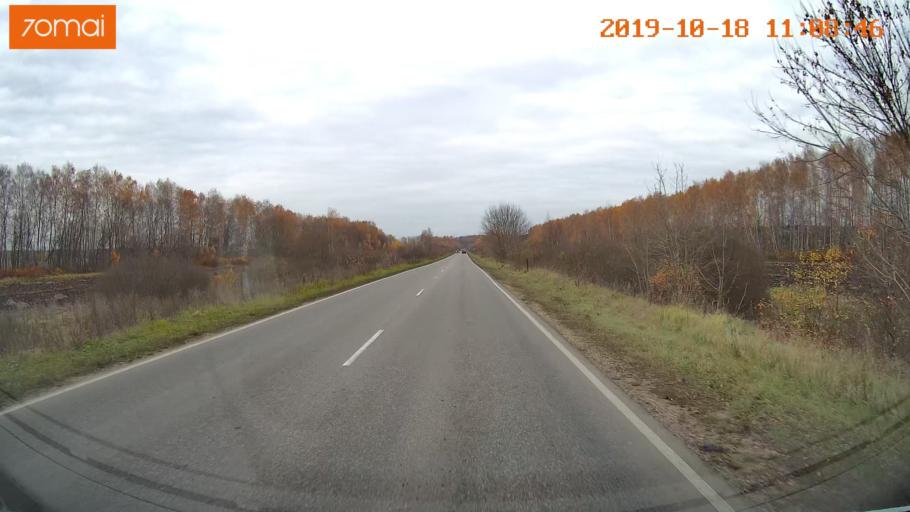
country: RU
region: Tula
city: Kimovsk
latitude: 53.9433
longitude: 38.5352
